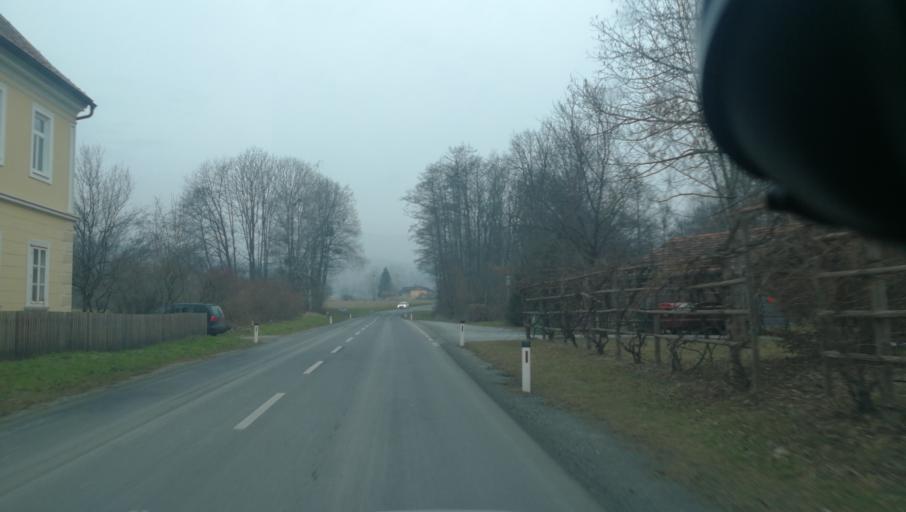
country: AT
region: Styria
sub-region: Politischer Bezirk Deutschlandsberg
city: Greisdorf
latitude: 46.9040
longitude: 15.2404
